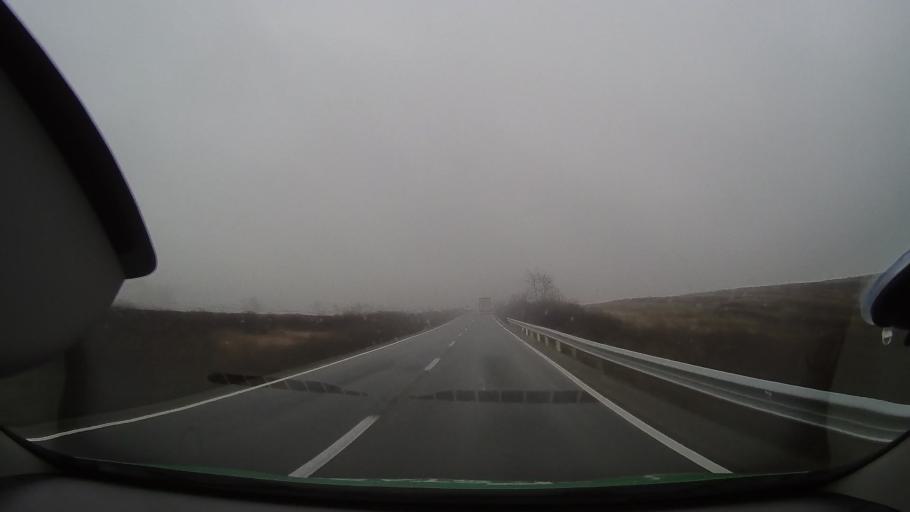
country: RO
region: Bihor
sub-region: Comuna Olcea
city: Olcea
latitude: 46.6783
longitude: 21.9657
